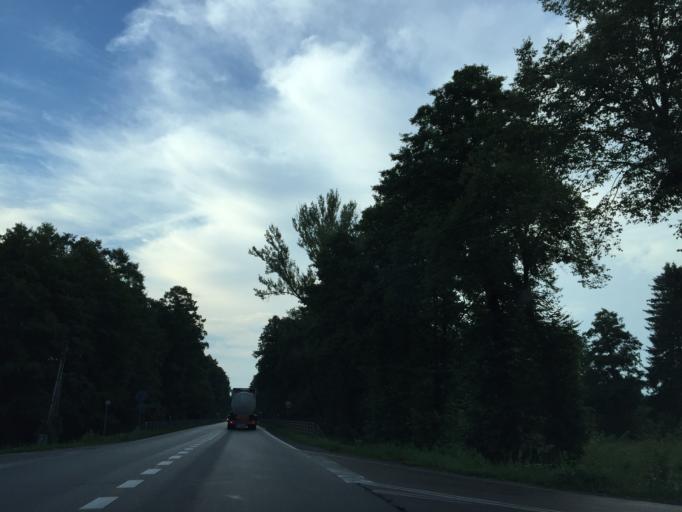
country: PL
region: Masovian Voivodeship
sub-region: Powiat wegrowski
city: Sadowne
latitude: 52.6414
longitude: 21.8453
